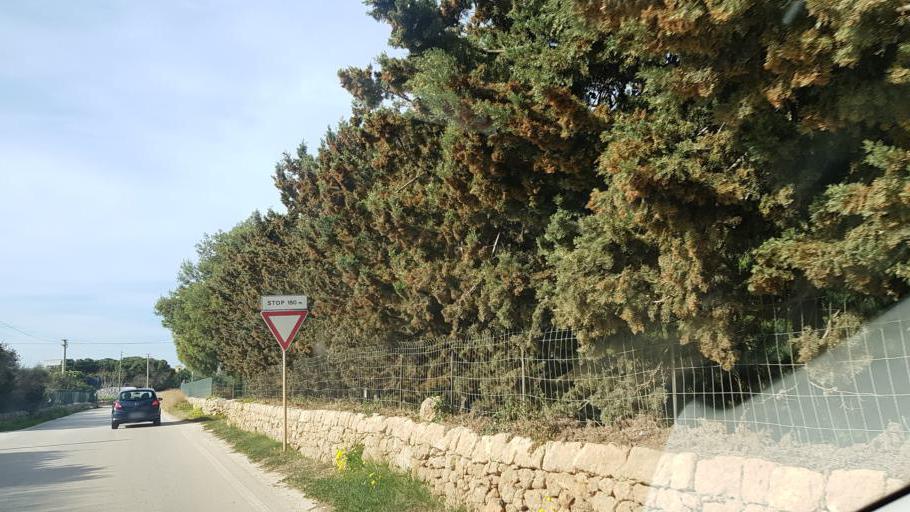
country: IT
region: Apulia
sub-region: Provincia di Brindisi
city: Fasano
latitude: 40.9029
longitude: 17.3511
